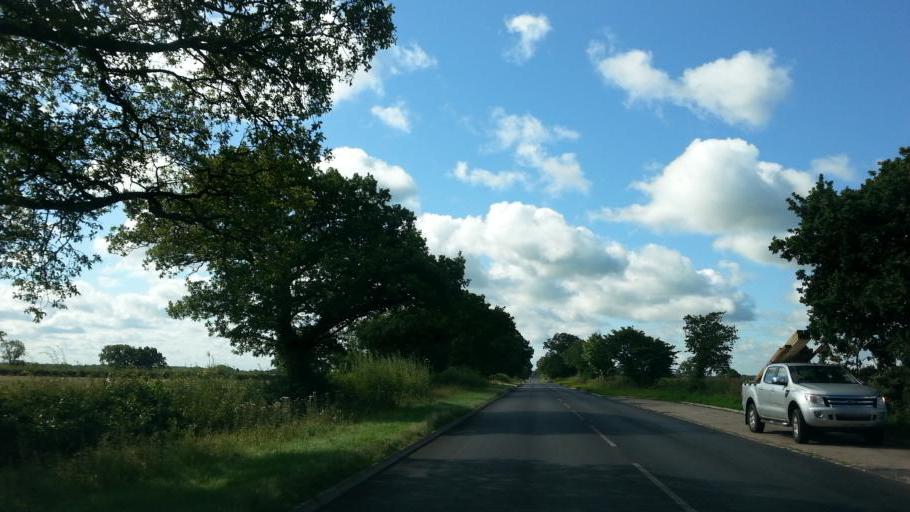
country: GB
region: England
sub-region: Staffordshire
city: Barton under Needwood
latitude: 52.8325
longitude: -1.7791
